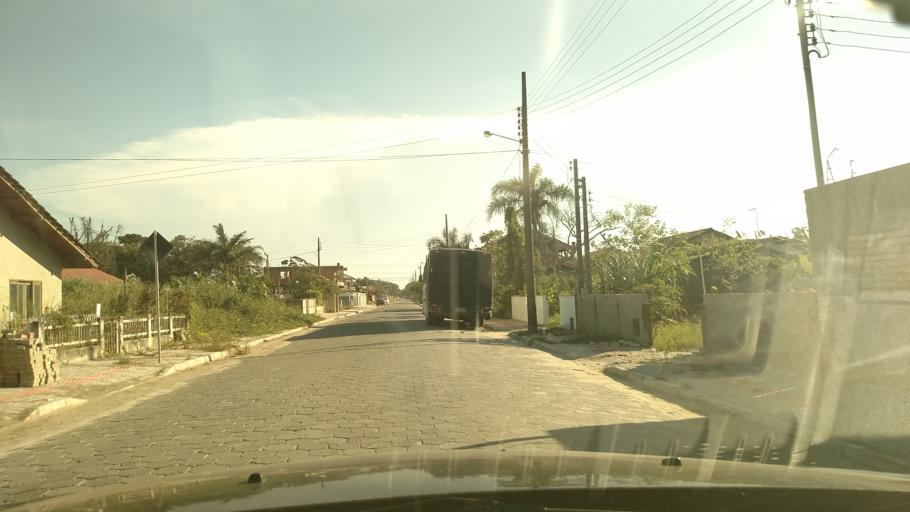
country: BR
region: Santa Catarina
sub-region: Porto Belo
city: Porto Belo
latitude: -27.1760
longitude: -48.5056
